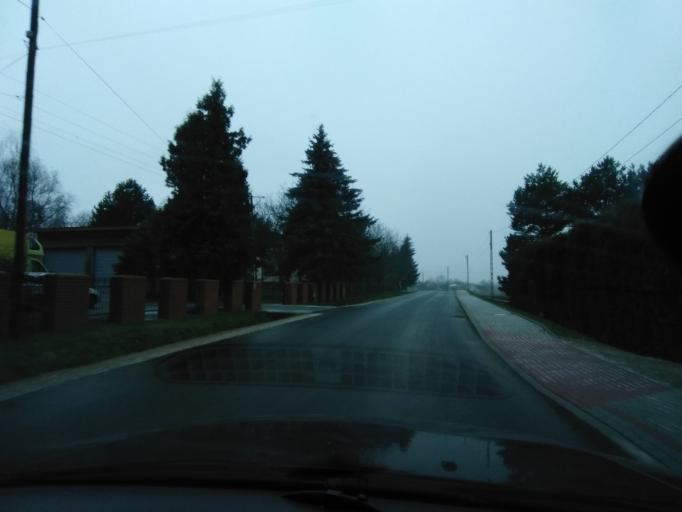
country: PL
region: Subcarpathian Voivodeship
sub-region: Powiat przeworski
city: Kanczuga
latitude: 50.0134
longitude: 22.4212
